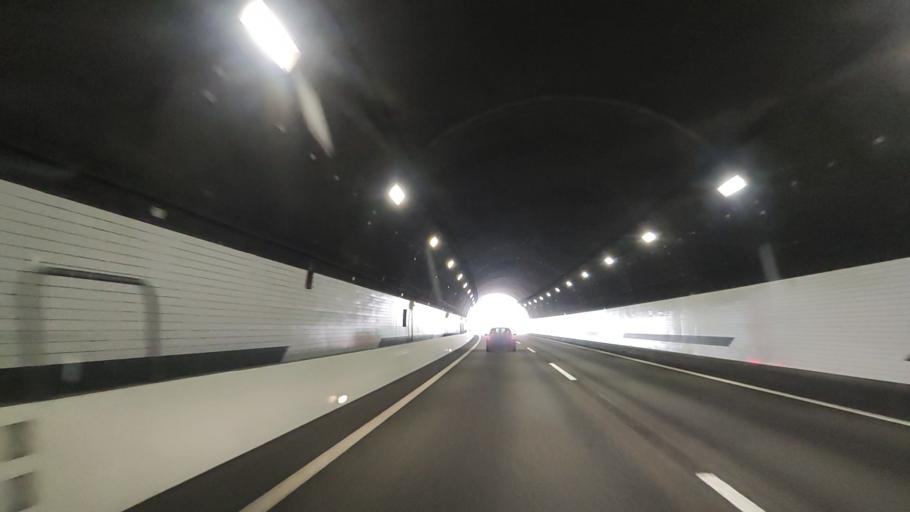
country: JP
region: Tokushima
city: Ishii
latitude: 34.1970
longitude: 134.4317
